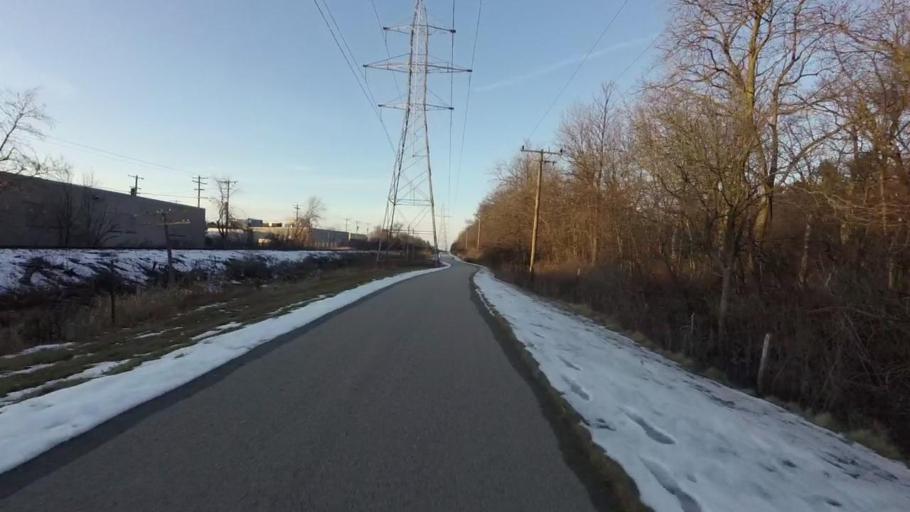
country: US
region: Wisconsin
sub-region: Milwaukee County
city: Brown Deer
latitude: 43.1501
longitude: -87.9552
